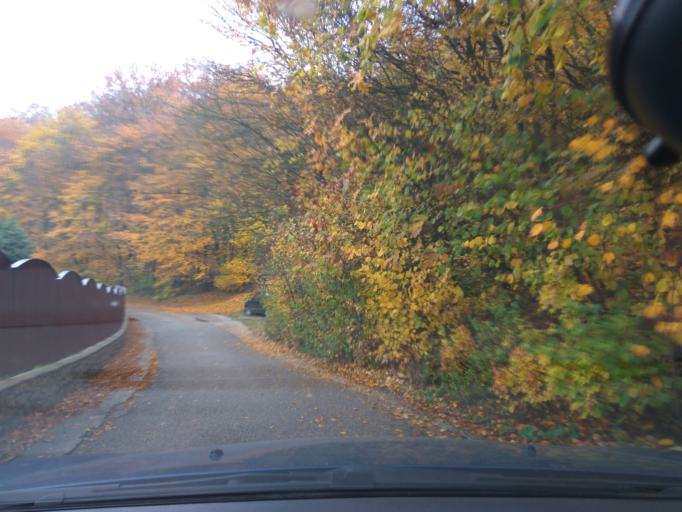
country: SK
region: Trnavsky
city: Vrbove
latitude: 48.6853
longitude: 17.7015
